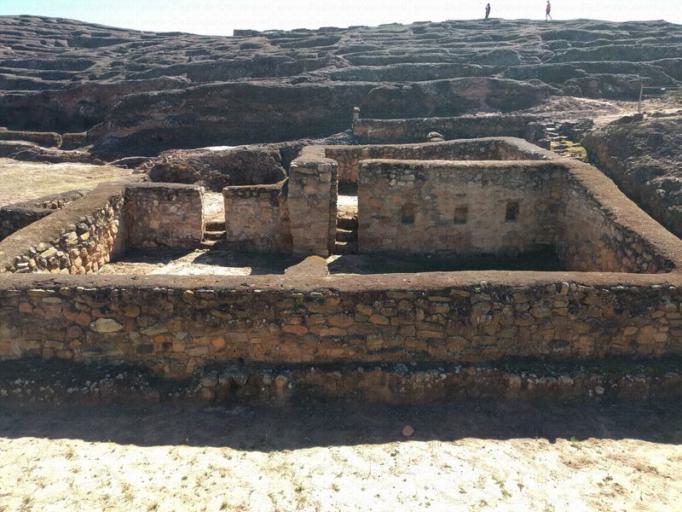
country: BO
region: Santa Cruz
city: Samaipata
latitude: -18.1790
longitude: -63.8189
